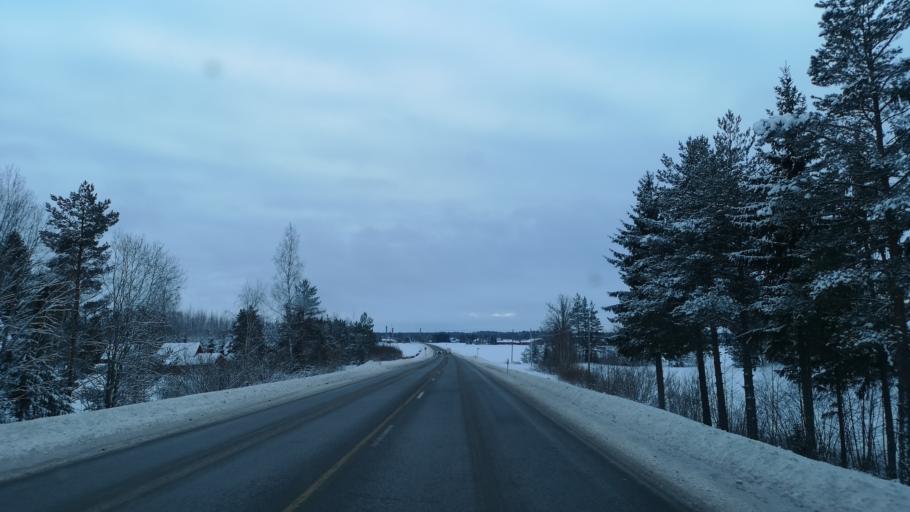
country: FI
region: Varsinais-Suomi
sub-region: Loimaa
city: Loimaa
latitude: 60.8685
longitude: 23.0574
